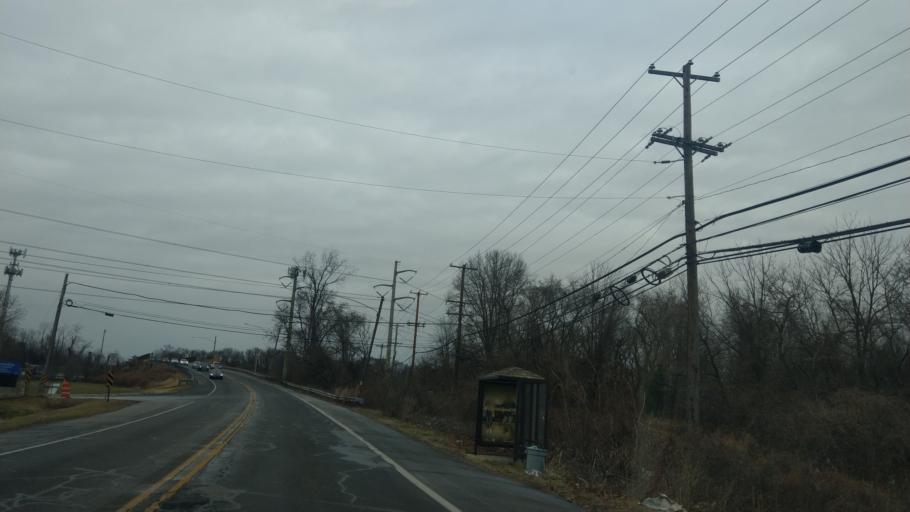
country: US
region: Pennsylvania
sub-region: Bucks County
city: Bristol
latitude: 40.1228
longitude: -74.8641
